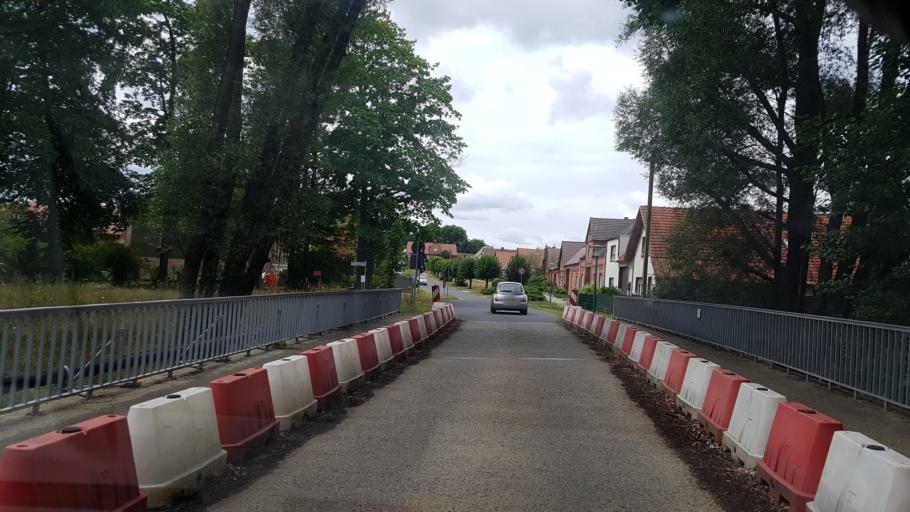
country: DE
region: Brandenburg
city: Spremberg
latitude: 51.5082
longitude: 14.4031
